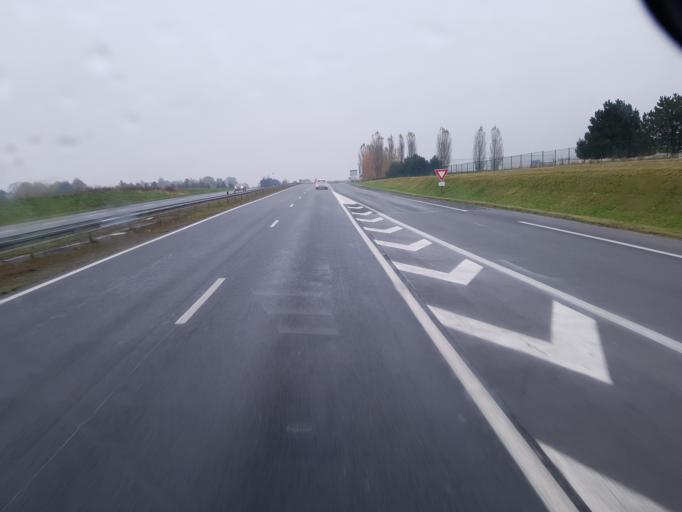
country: FR
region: Picardie
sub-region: Departement de l'Aisne
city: Gauchy
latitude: 49.8156
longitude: 3.2910
